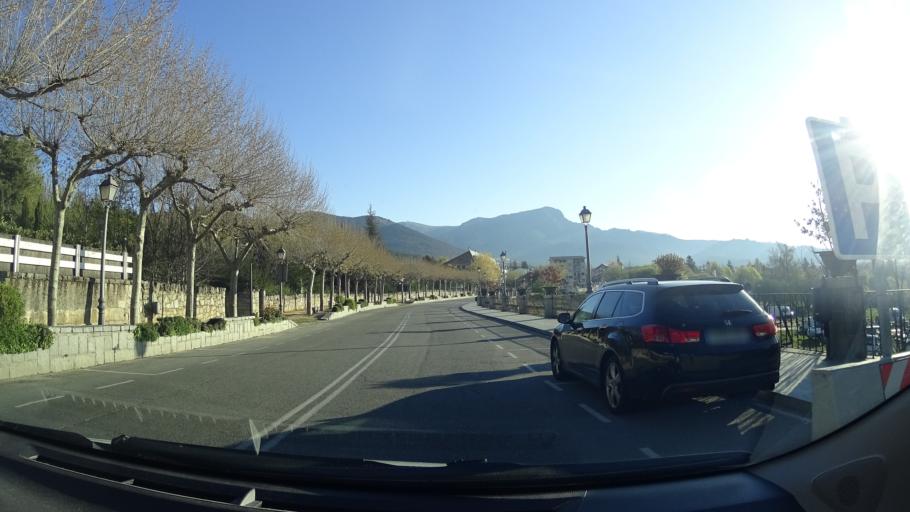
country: ES
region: Madrid
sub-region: Provincia de Madrid
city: Navacerrada
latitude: 40.7264
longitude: -4.0189
